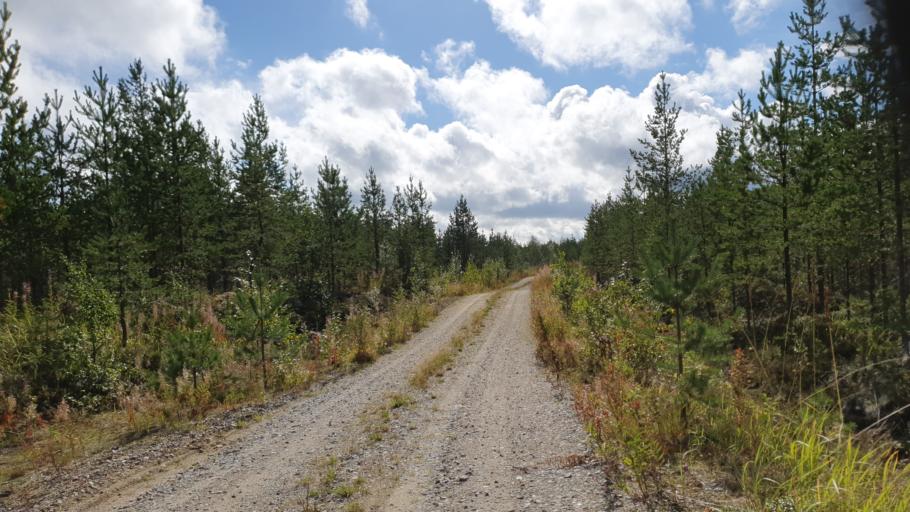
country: FI
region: Kainuu
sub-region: Kehys-Kainuu
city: Kuhmo
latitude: 64.1489
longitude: 29.3889
